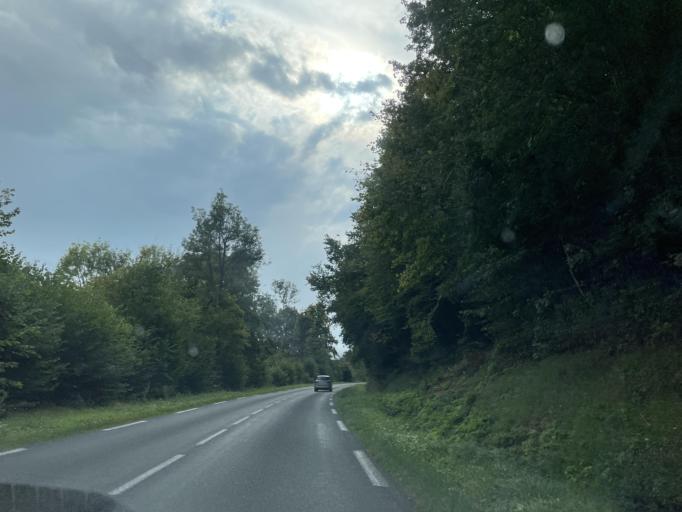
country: FR
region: Haute-Normandie
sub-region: Departement de la Seine-Maritime
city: Neufchatel-en-Bray
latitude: 49.7757
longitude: 1.4418
